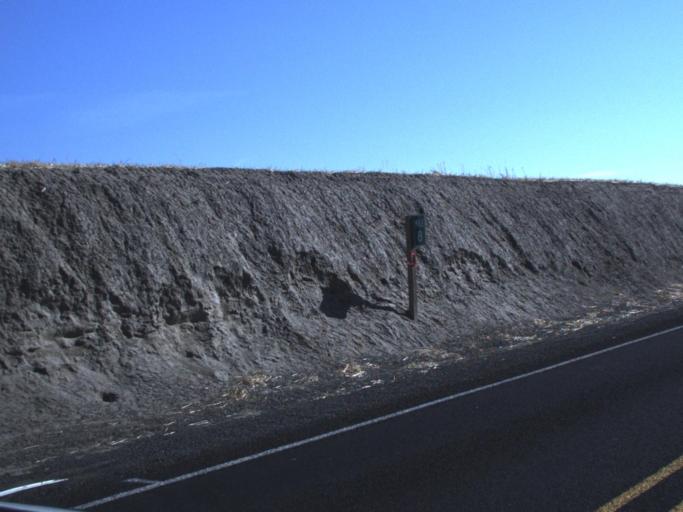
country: US
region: Washington
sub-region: Walla Walla County
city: Walla Walla
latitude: 46.0900
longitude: -118.3674
